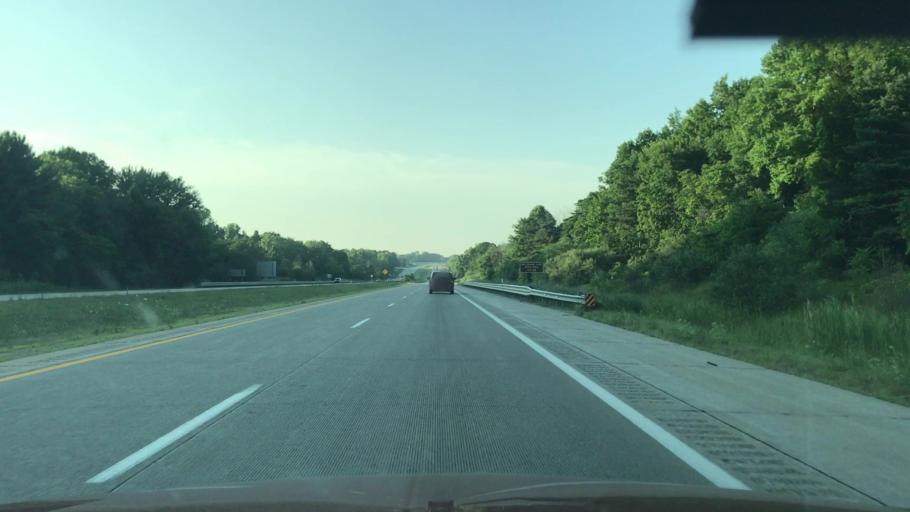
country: US
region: Michigan
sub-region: Van Buren County
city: South Haven
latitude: 42.4126
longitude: -86.2522
